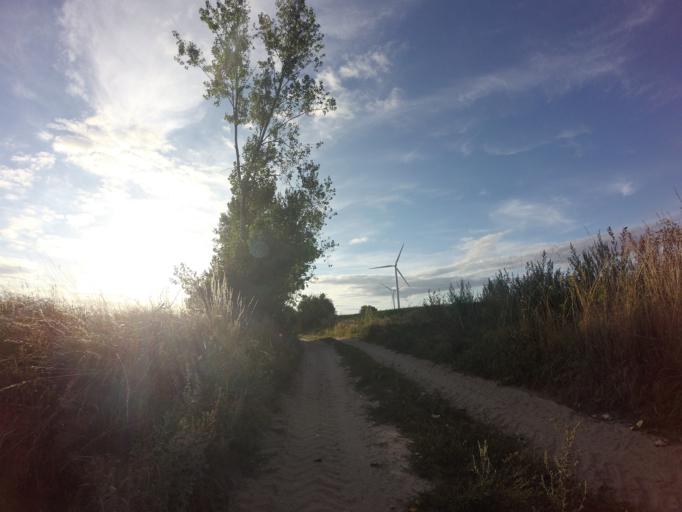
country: PL
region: West Pomeranian Voivodeship
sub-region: Powiat choszczenski
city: Krzecin
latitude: 53.1117
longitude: 15.4406
